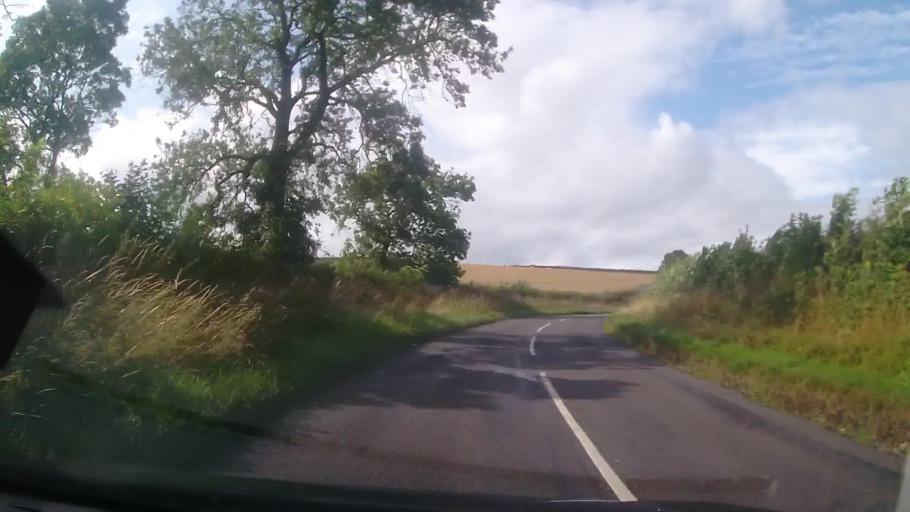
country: GB
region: Wales
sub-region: Sir Powys
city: Knighton
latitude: 52.3890
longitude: -3.0405
